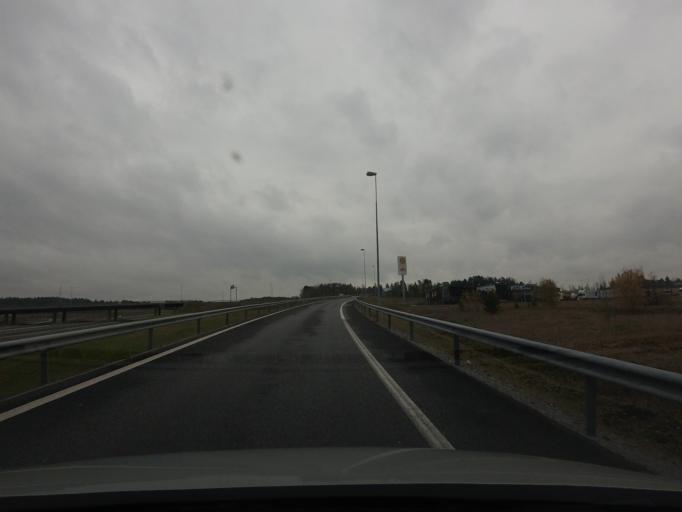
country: FI
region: Varsinais-Suomi
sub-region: Salo
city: Halikko
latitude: 60.4267
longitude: 23.0427
